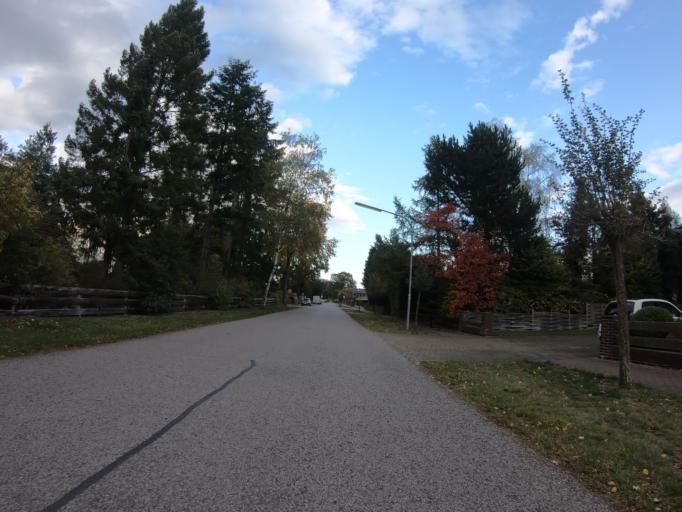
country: DE
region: Lower Saxony
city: Wagenhoff
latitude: 52.5546
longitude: 10.5235
